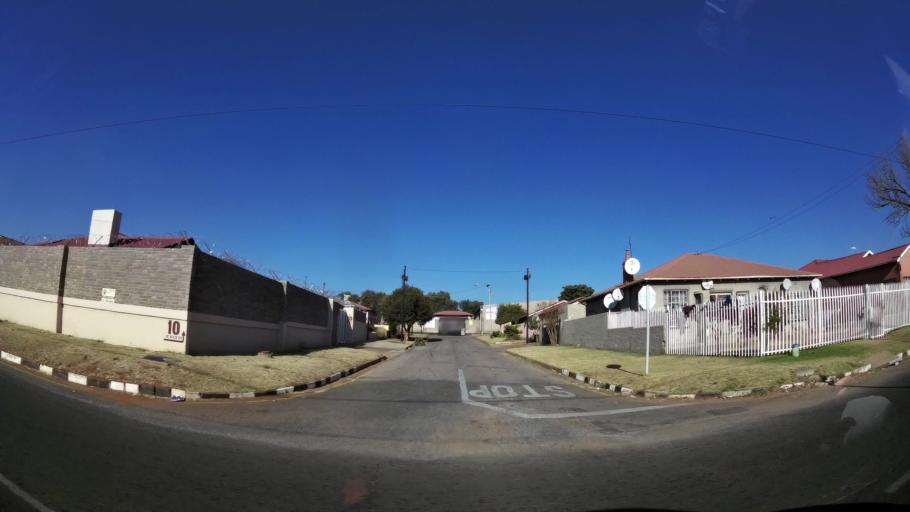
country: ZA
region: Gauteng
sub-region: City of Johannesburg Metropolitan Municipality
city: Roodepoort
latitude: -26.1655
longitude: 27.8729
